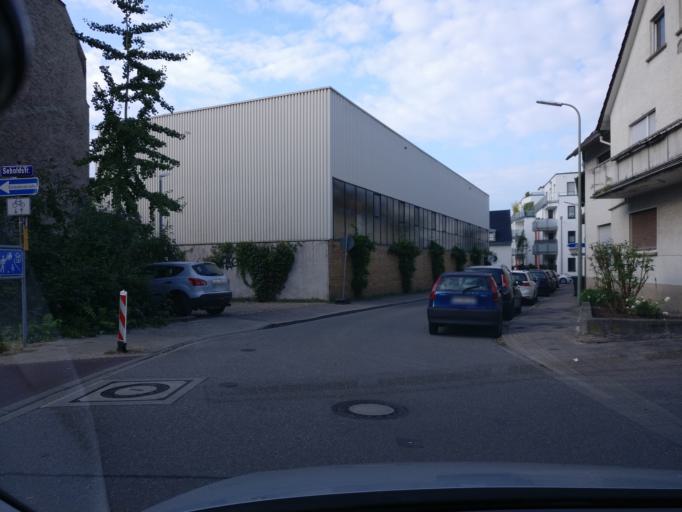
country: DE
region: Baden-Wuerttemberg
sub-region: Karlsruhe Region
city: Karlsruhe
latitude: 49.0011
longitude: 8.4697
